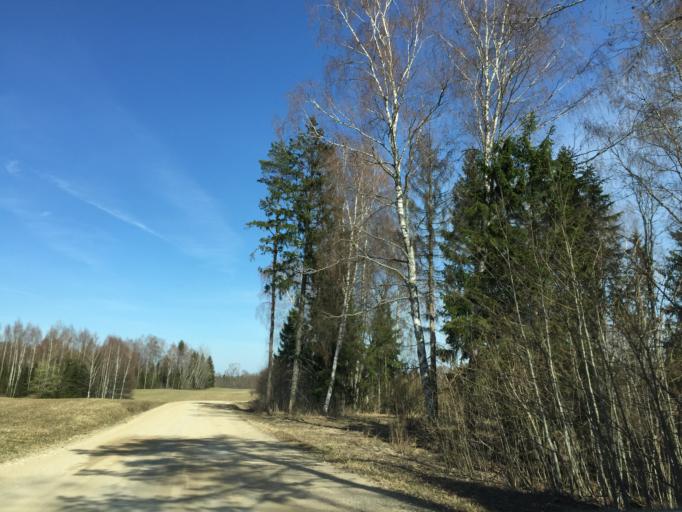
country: EE
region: Vorumaa
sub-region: Antsla vald
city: Vana-Antsla
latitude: 57.9866
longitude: 26.3611
